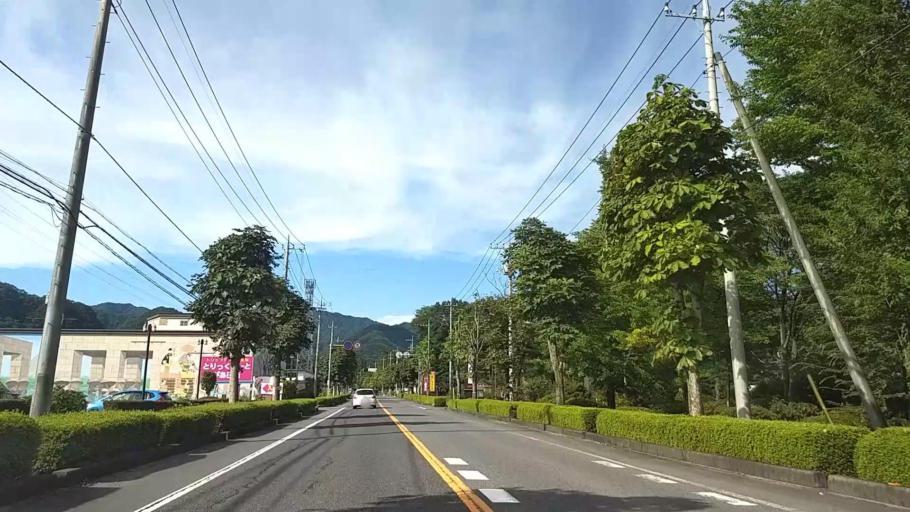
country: JP
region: Tochigi
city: Imaichi
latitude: 36.7883
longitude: 139.7022
